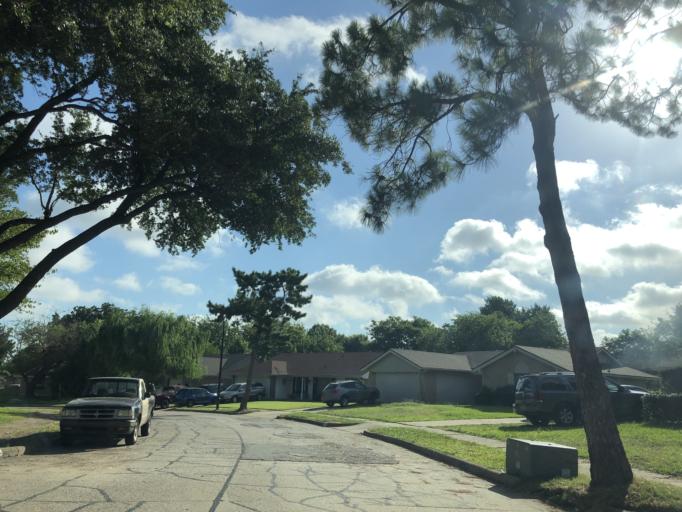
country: US
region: Texas
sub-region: Dallas County
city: Garland
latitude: 32.8619
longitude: -96.6339
